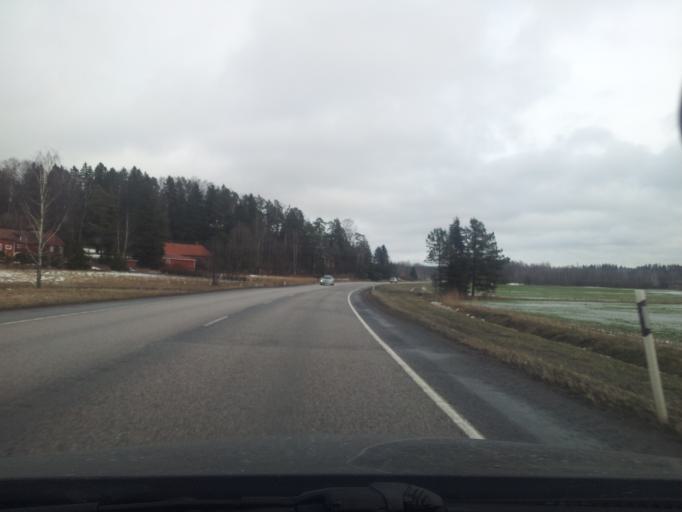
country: FI
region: Uusimaa
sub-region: Helsinki
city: Espoo
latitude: 60.1826
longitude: 24.5615
